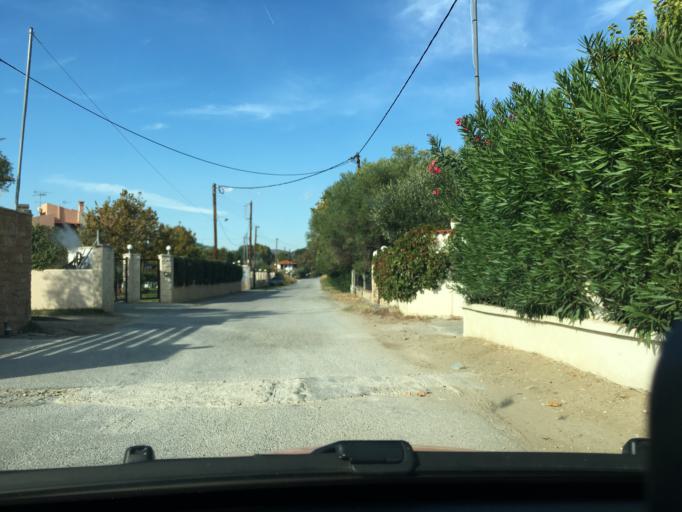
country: GR
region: Central Macedonia
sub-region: Nomos Chalkidikis
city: Agios Nikolaos
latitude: 40.2921
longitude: 23.6937
